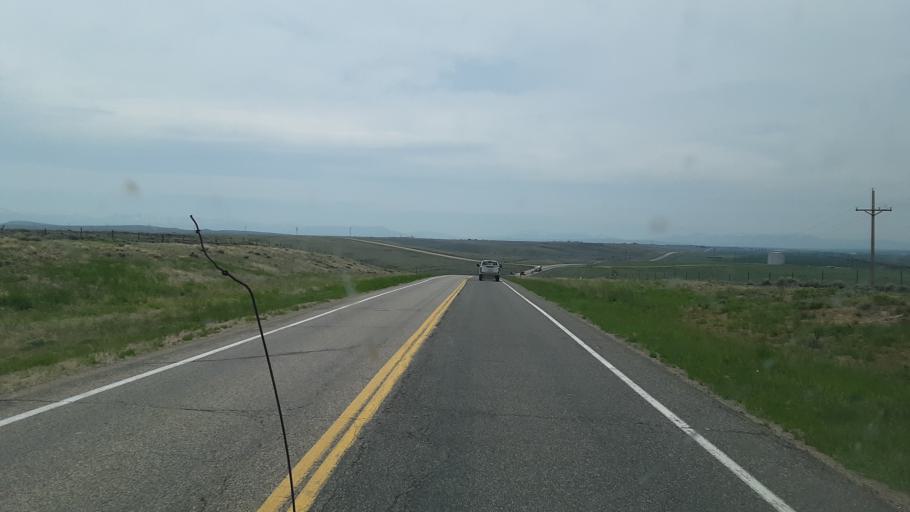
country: US
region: Colorado
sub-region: Jackson County
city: Walden
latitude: 40.7913
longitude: -106.2828
